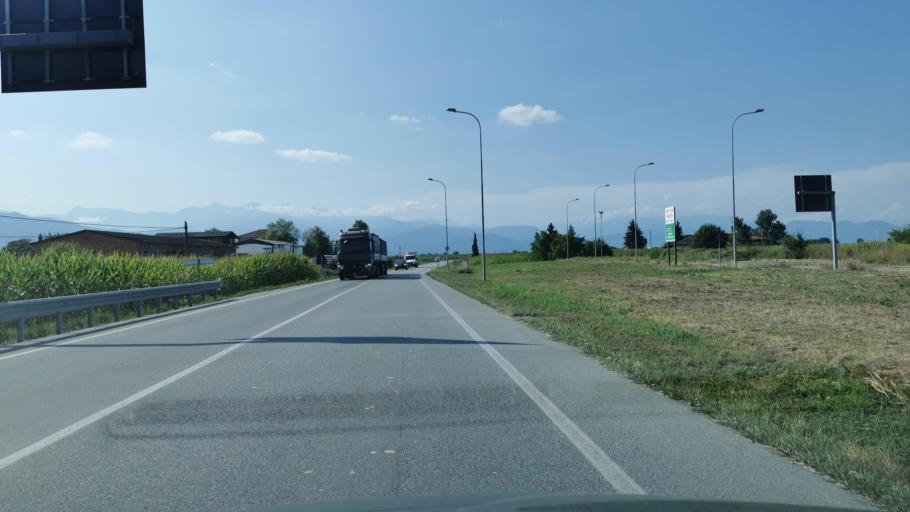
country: IT
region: Piedmont
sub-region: Provincia di Cuneo
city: Carde
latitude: 44.7354
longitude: 7.4203
